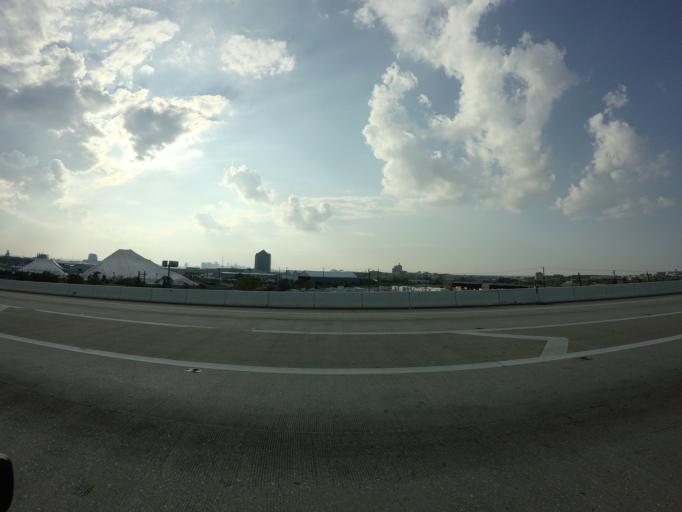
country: US
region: Maryland
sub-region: Baltimore County
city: Dundalk
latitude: 39.2704
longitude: -76.5575
